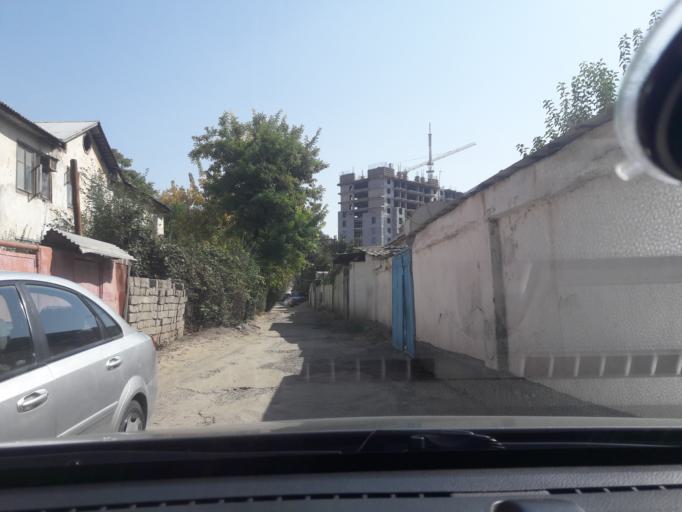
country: TJ
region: Dushanbe
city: Dushanbe
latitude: 38.5769
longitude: 68.7993
